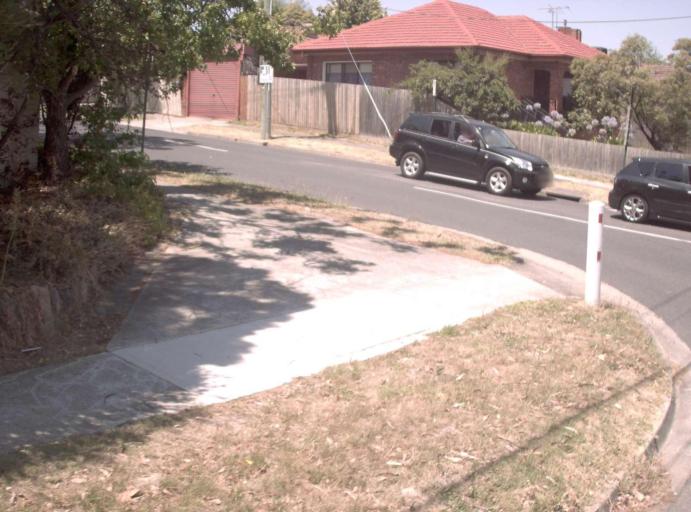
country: AU
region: Victoria
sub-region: Whitehorse
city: Forest Hill
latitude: -37.8382
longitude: 145.1721
